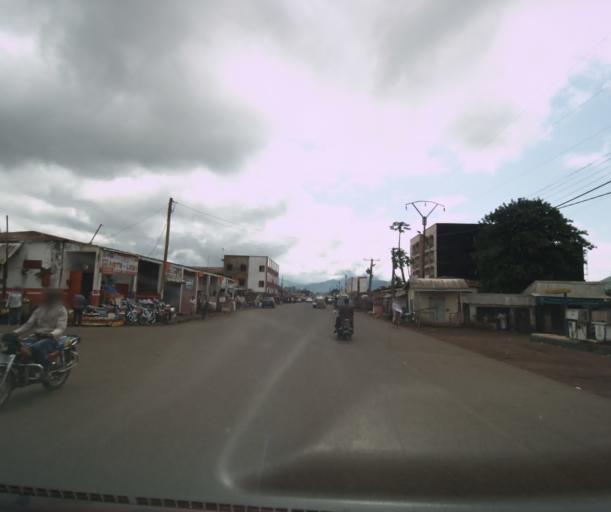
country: CM
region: West
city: Foumbot
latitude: 5.5092
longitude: 10.6341
